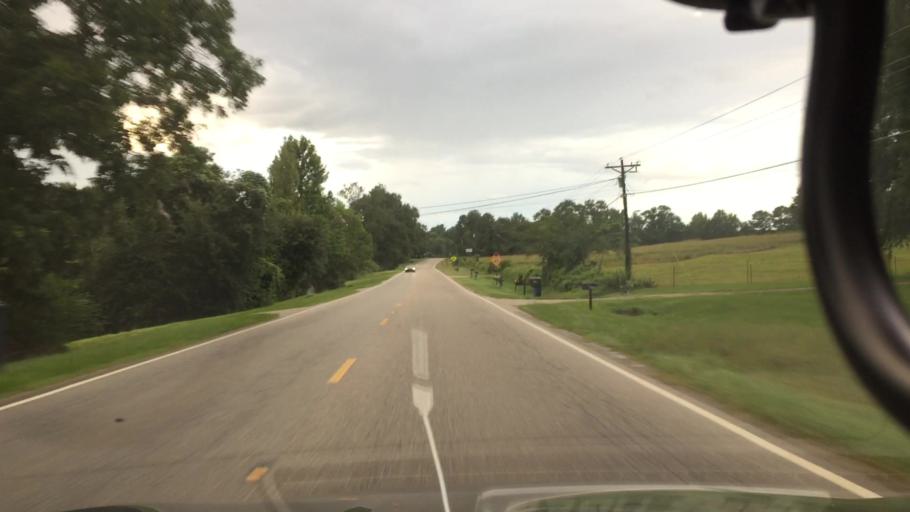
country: US
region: Alabama
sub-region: Pike County
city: Troy
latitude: 31.6993
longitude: -85.9591
